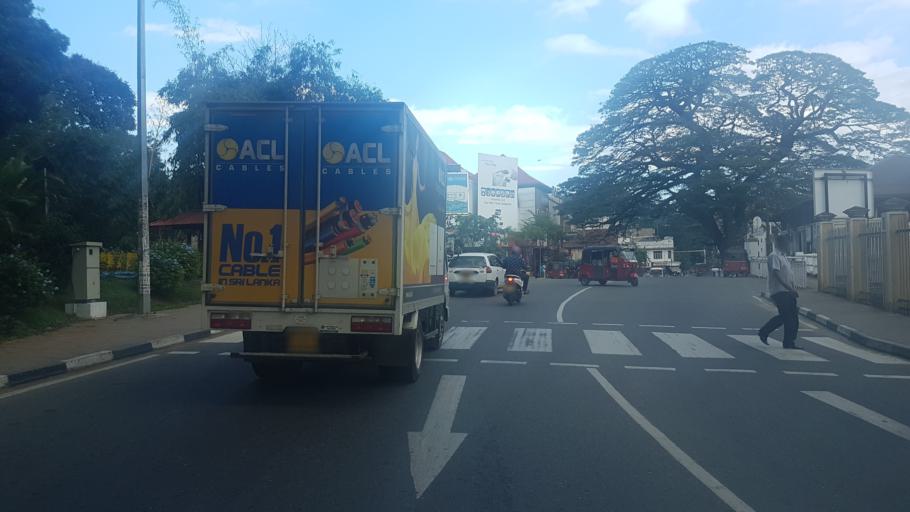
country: LK
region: Central
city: Kandy
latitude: 7.2930
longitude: 80.6331
